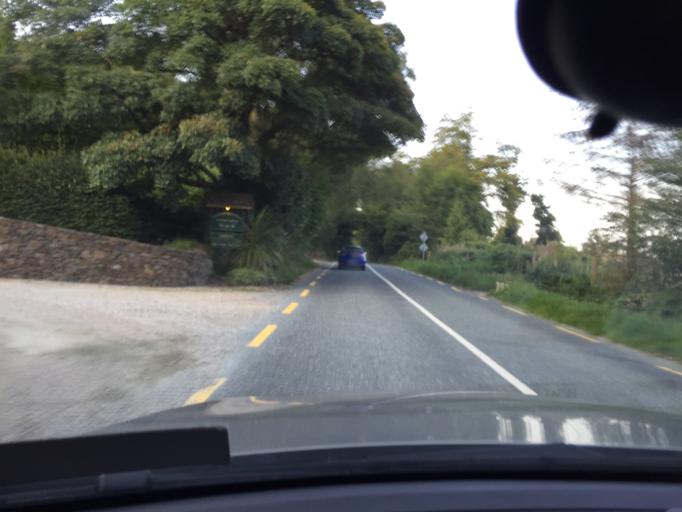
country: IE
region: Leinster
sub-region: Wicklow
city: Rathdrum
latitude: 53.0136
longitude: -6.2779
